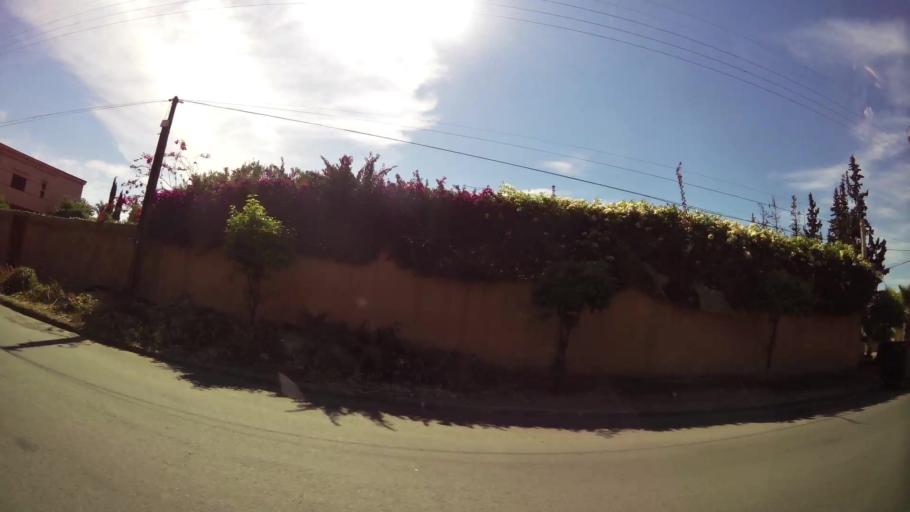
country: MA
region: Marrakech-Tensift-Al Haouz
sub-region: Marrakech
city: Marrakesh
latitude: 31.6449
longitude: -8.0472
